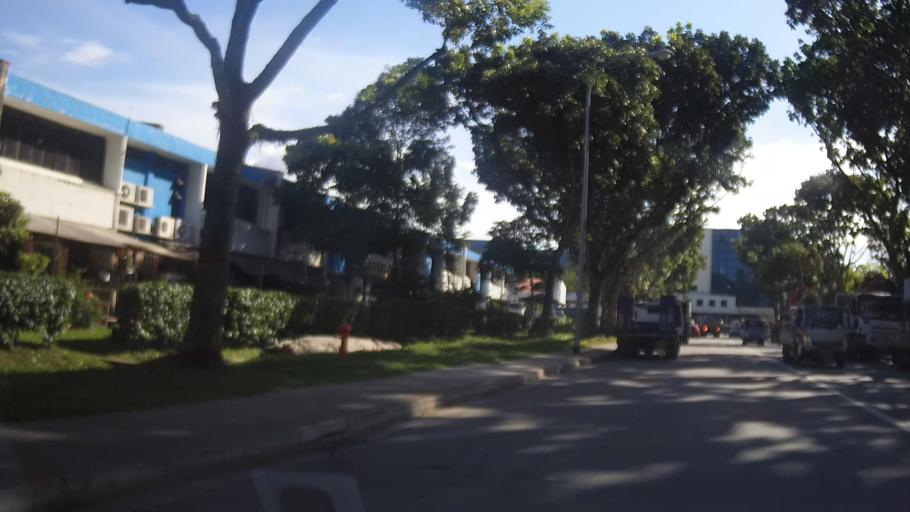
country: MY
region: Johor
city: Johor Bahru
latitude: 1.4333
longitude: 103.7570
